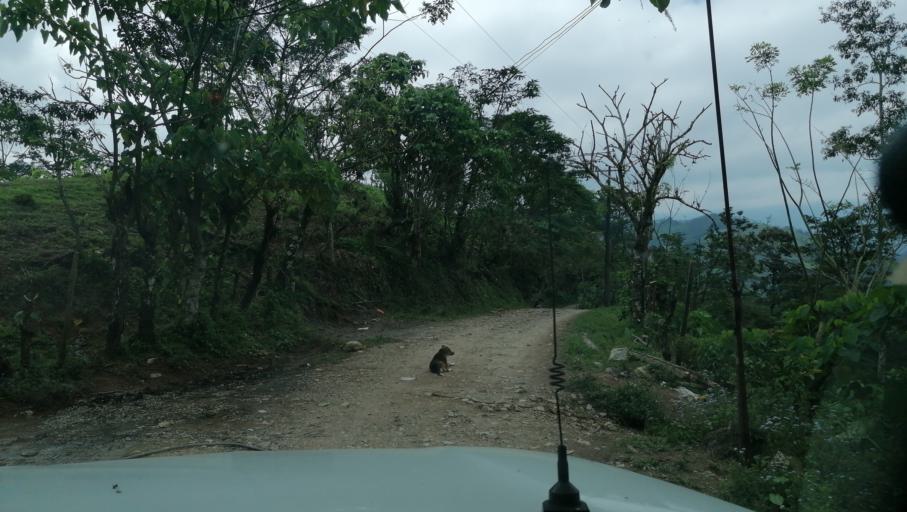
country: MX
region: Chiapas
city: Ixtacomitan
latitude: 17.3604
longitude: -93.1226
